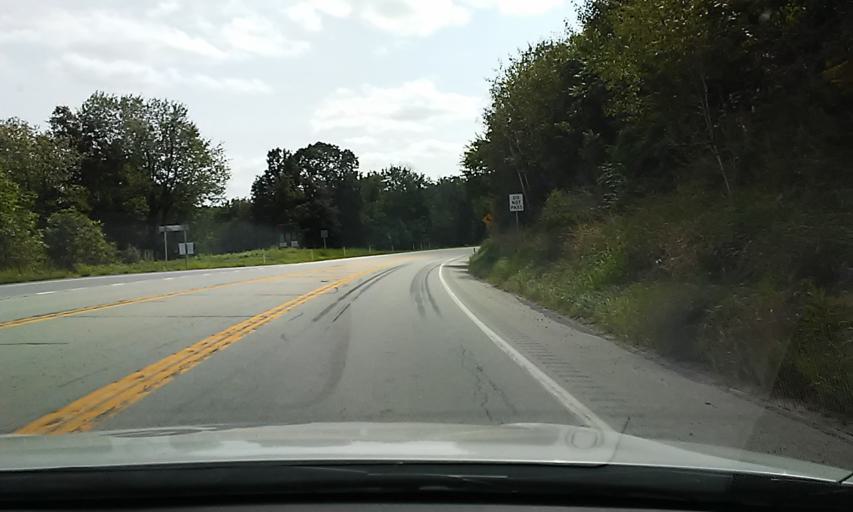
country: US
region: Pennsylvania
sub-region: Indiana County
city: Clymer
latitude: 40.7675
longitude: -79.0568
